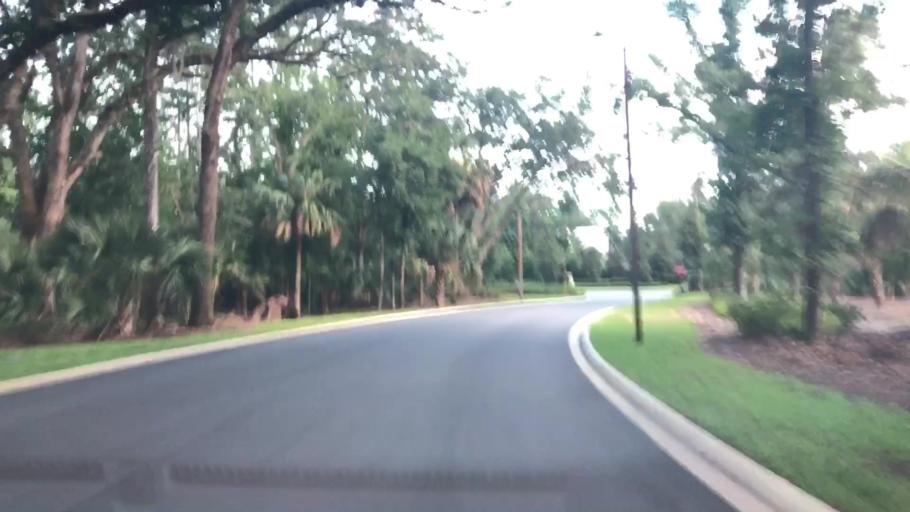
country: US
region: Florida
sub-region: Saint Johns County
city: Palm Valley
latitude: 30.1289
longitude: -81.4219
